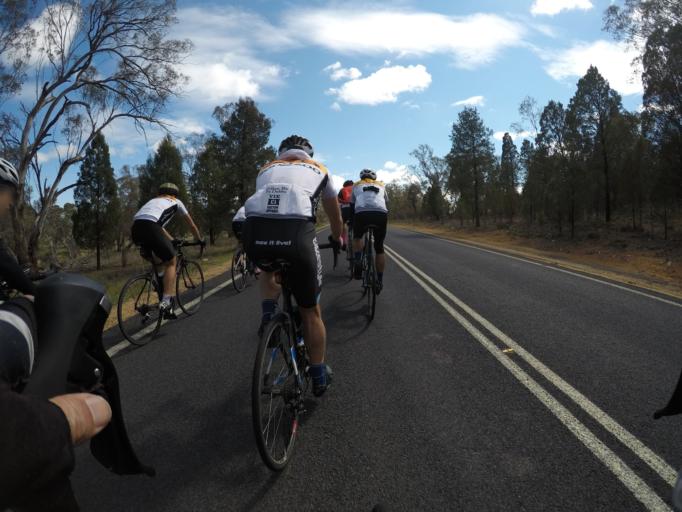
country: AU
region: New South Wales
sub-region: Parkes
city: Peak Hill
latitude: -32.6968
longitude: 148.5548
